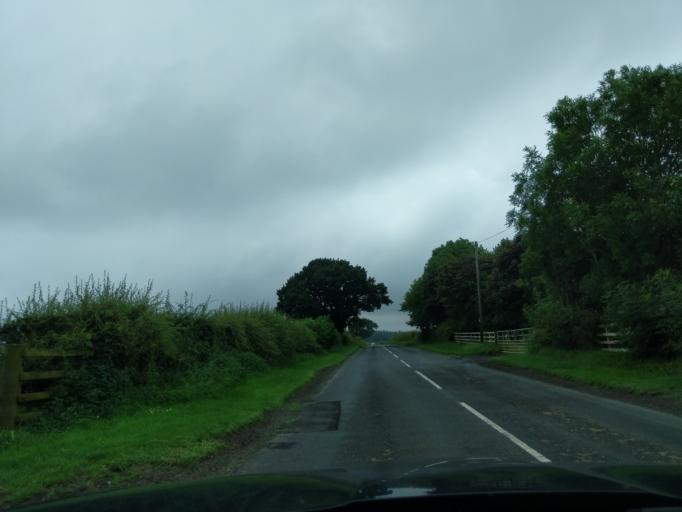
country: GB
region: England
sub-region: Northumberland
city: Ford
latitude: 55.6445
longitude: -2.0496
